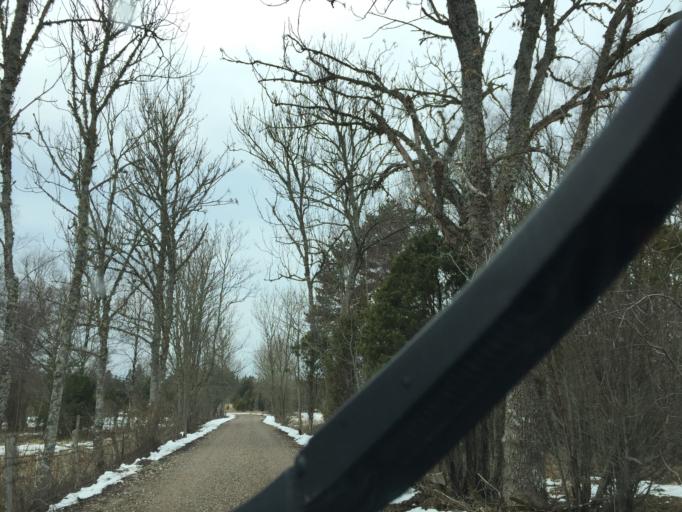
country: EE
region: Saare
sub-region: Kuressaare linn
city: Kuressaare
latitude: 58.4417
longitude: 22.1402
